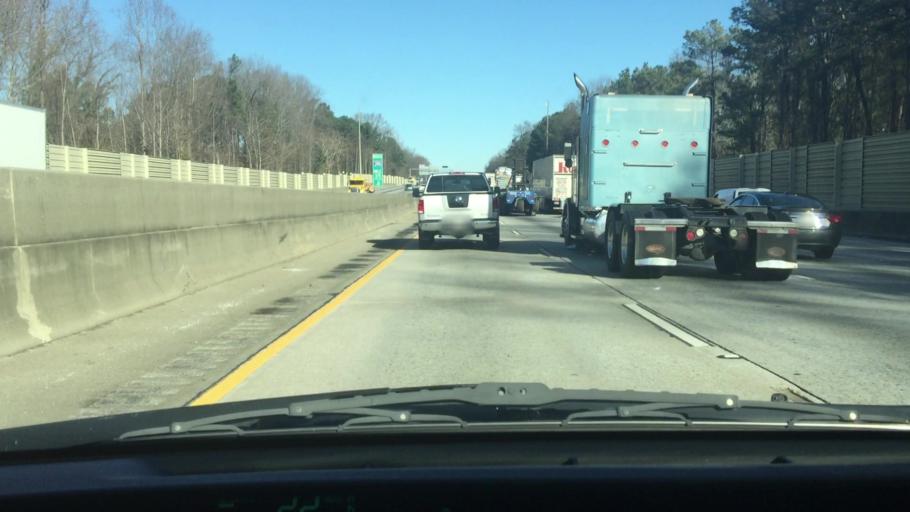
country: US
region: Georgia
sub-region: DeKalb County
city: Tucker
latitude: 33.8573
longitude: -84.2469
